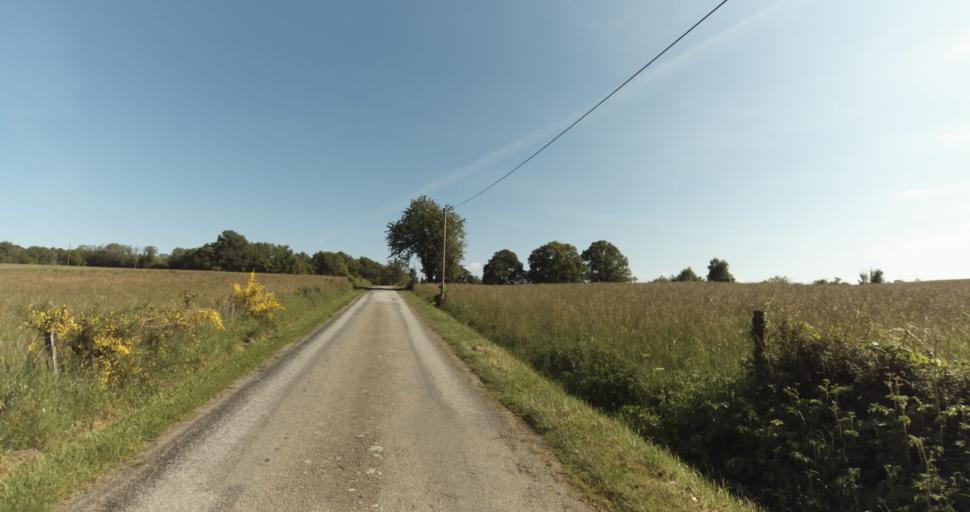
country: FR
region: Limousin
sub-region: Departement de la Haute-Vienne
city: Solignac
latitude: 45.7144
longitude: 1.2657
